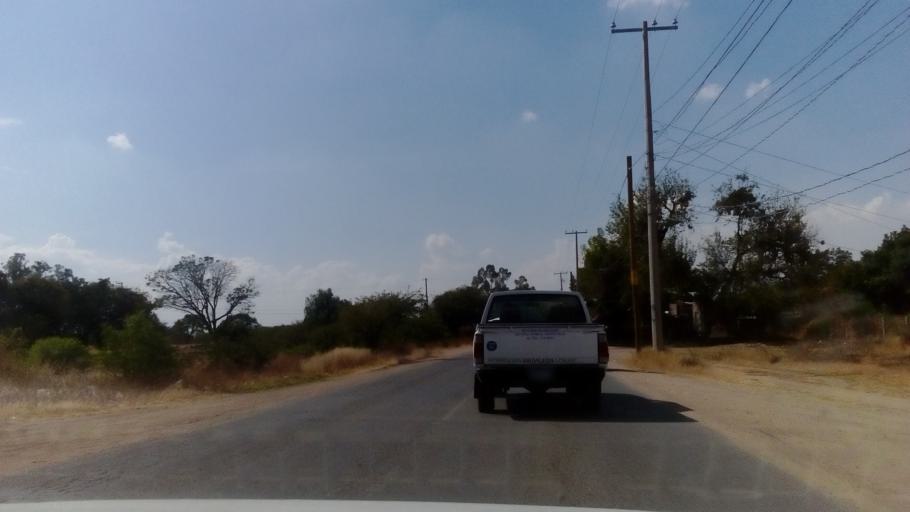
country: MX
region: Guanajuato
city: Duarte
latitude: 21.0887
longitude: -101.5301
